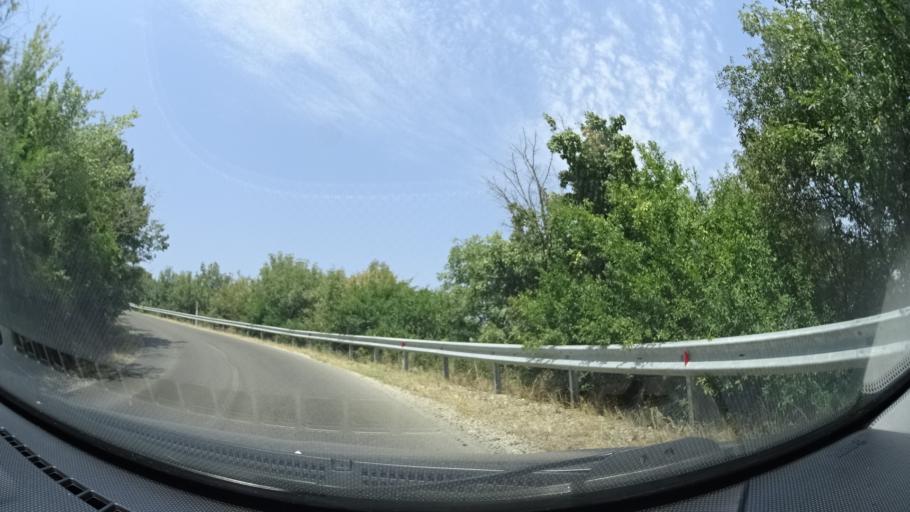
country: GE
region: Kakheti
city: Sighnaghi
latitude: 41.6240
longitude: 45.9346
